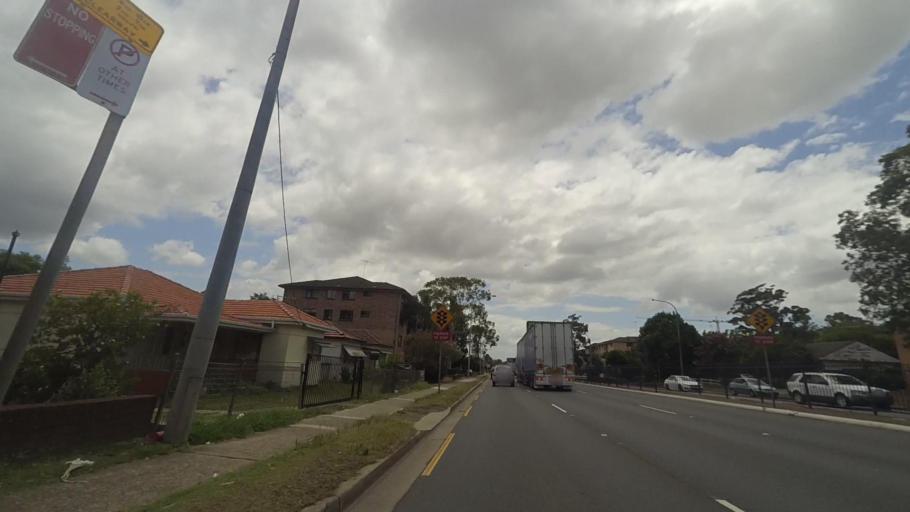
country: AU
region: New South Wales
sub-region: Fairfield
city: Liverpool
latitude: -33.9217
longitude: 150.9189
